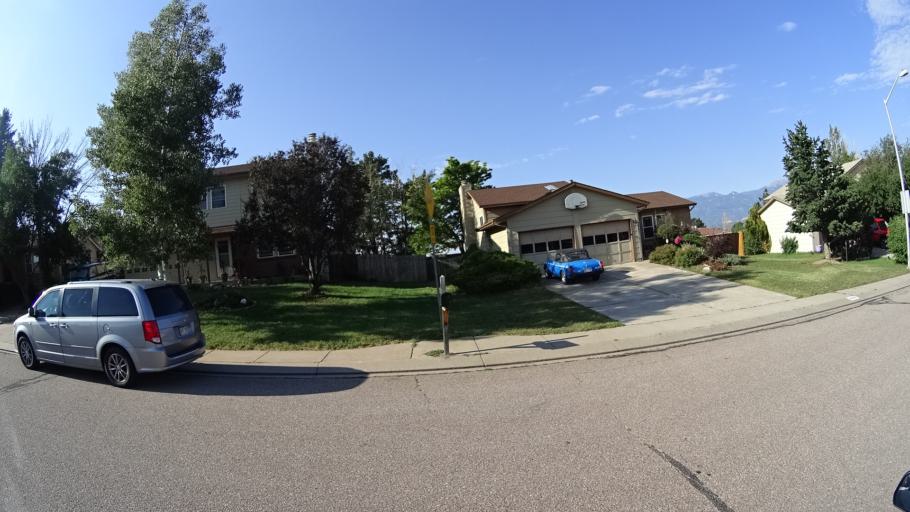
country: US
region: Colorado
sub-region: El Paso County
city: Black Forest
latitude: 38.9439
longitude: -104.7728
